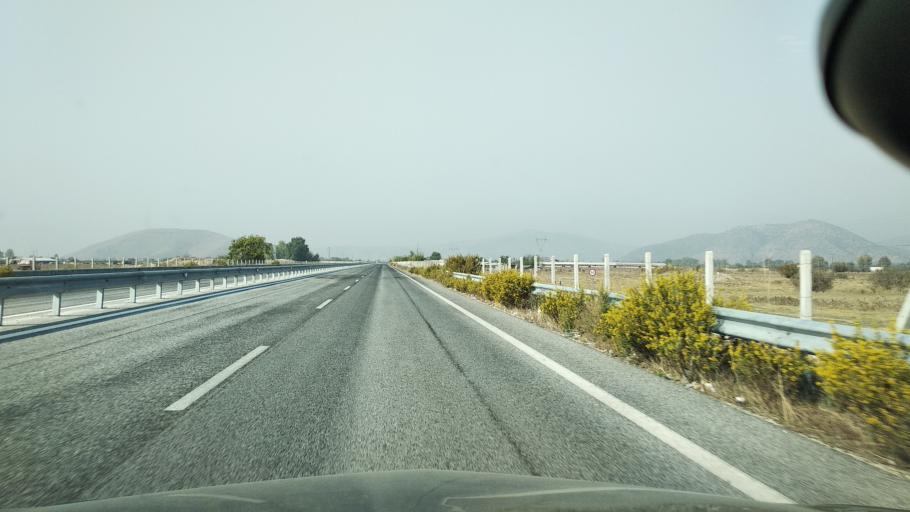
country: GR
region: Thessaly
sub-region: Trikala
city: Farkadona
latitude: 39.5832
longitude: 22.0609
